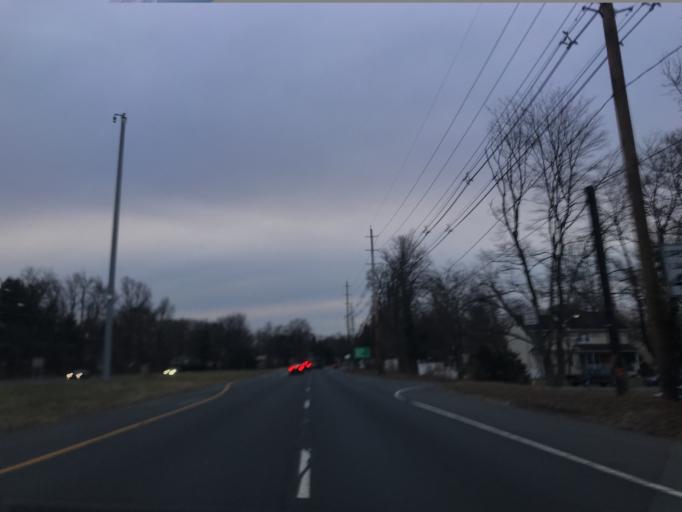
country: US
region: New Jersey
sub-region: Middlesex County
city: Milltown
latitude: 40.4539
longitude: -74.4582
